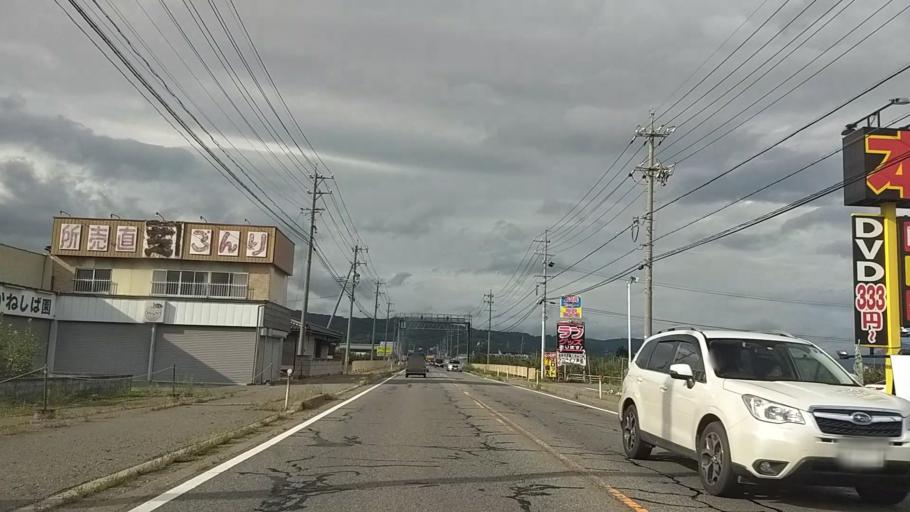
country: JP
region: Nagano
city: Suzaka
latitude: 36.6851
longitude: 138.2679
